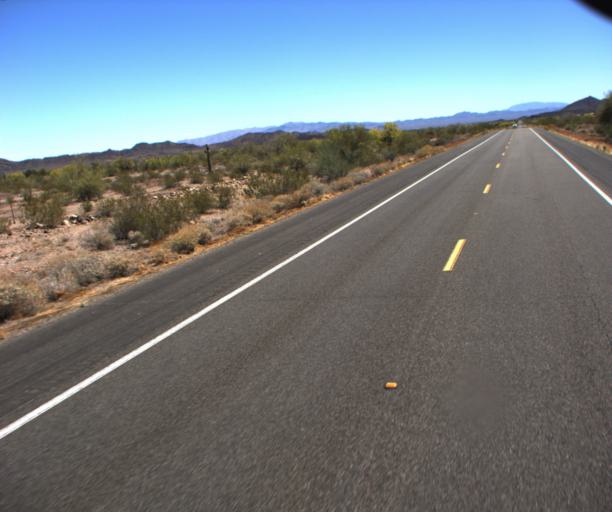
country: US
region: Arizona
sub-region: La Paz County
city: Quartzsite
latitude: 33.6704
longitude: -113.9825
